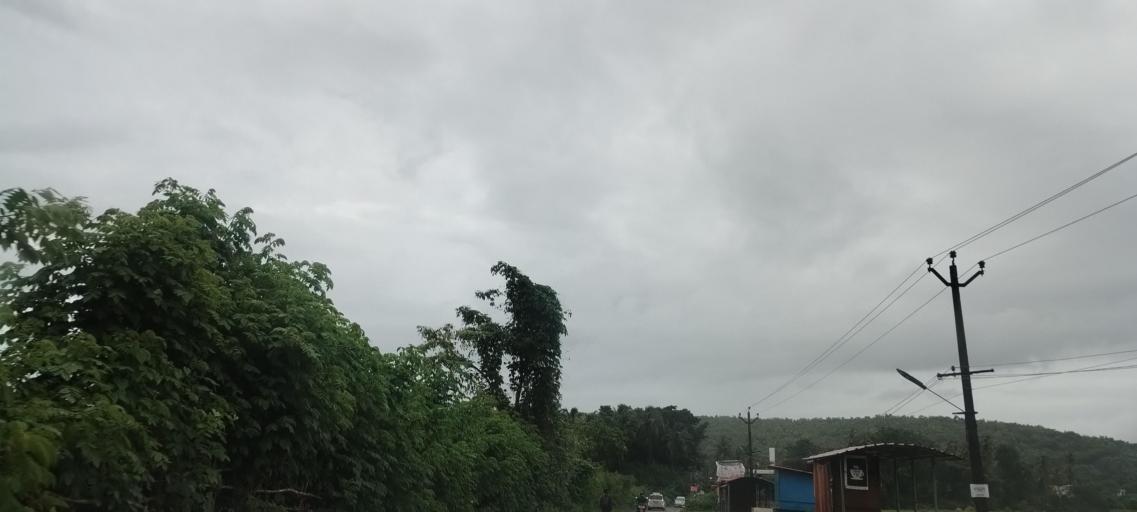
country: IN
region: Goa
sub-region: North Goa
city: Solim
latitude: 15.5931
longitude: 73.7719
